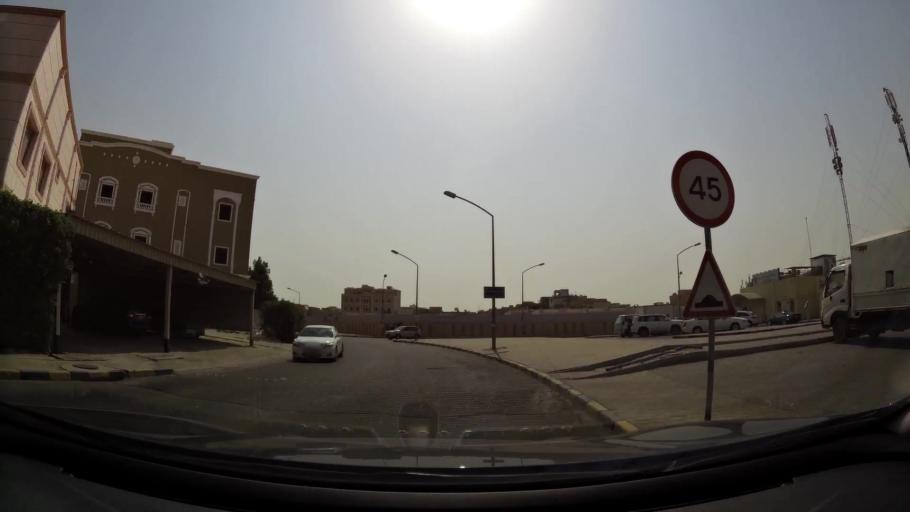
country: KW
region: Muhafazat al Jahra'
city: Al Jahra'
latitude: 29.3210
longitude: 47.6772
